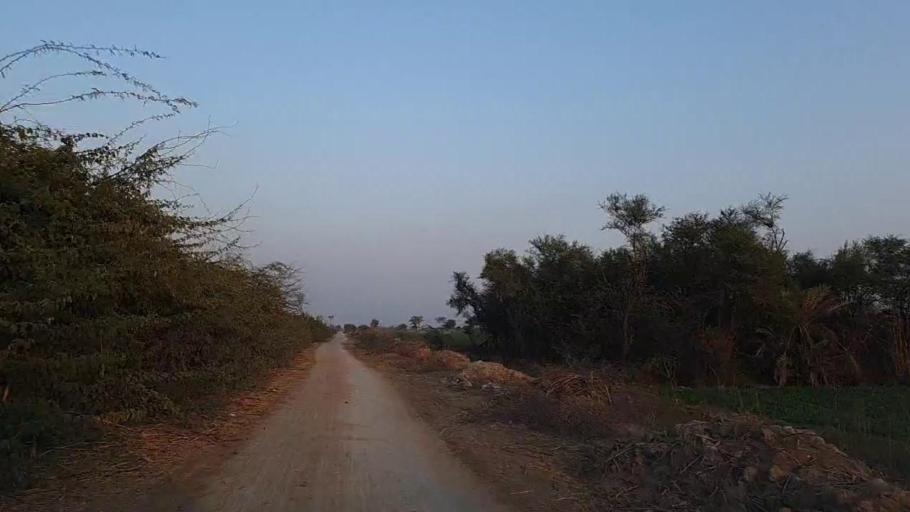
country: PK
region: Sindh
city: Jam Sahib
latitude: 26.3051
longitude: 68.5601
